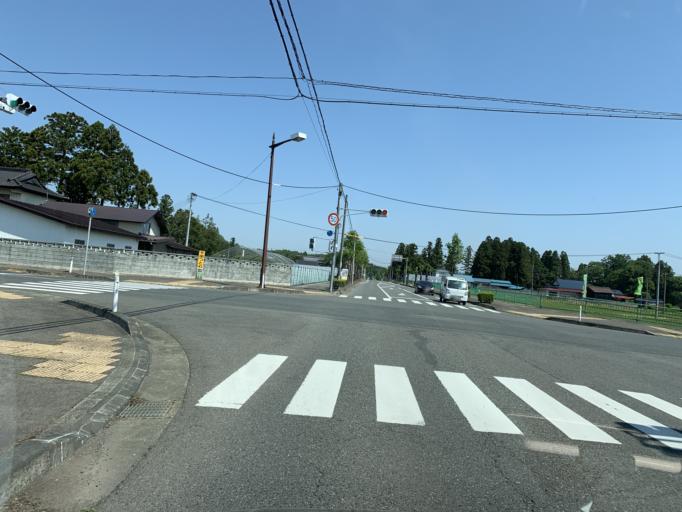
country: JP
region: Iwate
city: Mizusawa
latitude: 39.2010
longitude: 141.0950
